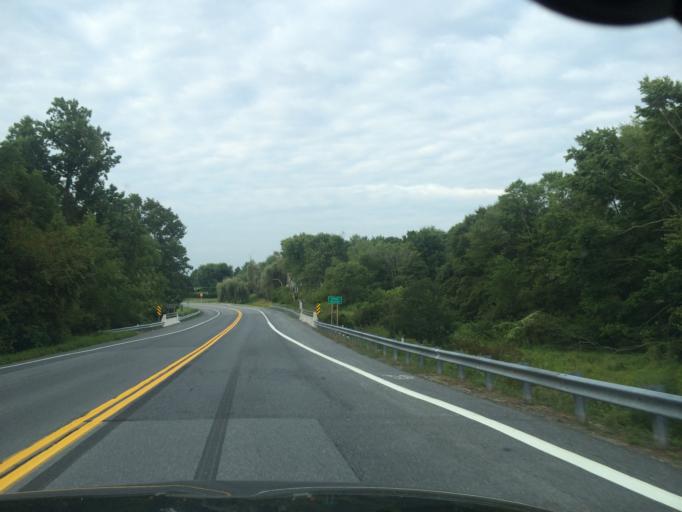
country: US
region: Maryland
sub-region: Carroll County
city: Sykesville
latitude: 39.3963
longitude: -77.0176
